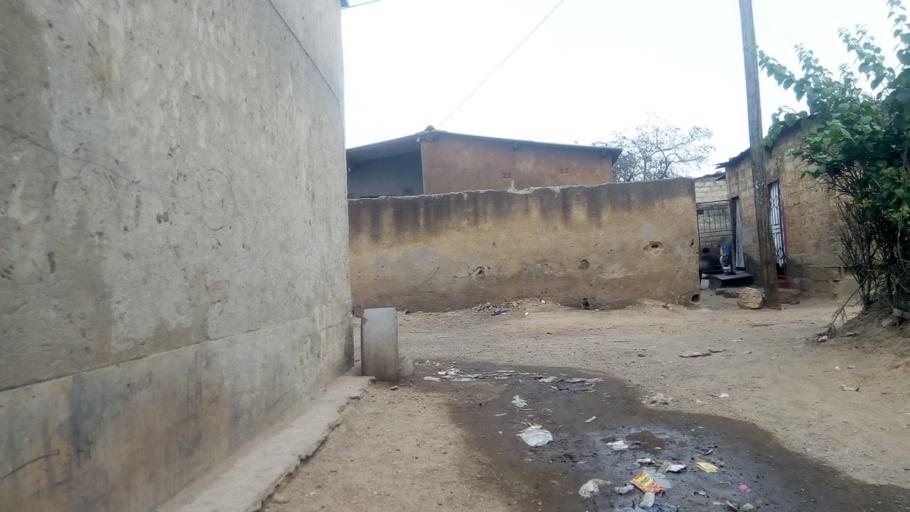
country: ZM
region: Lusaka
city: Lusaka
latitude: -15.3630
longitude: 28.2933
